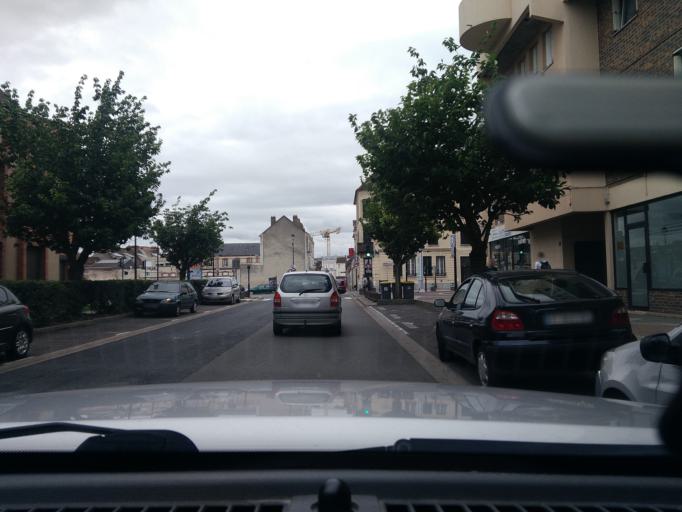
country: FR
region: Ile-de-France
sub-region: Departement de Seine-et-Marne
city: Montereau-Fault-Yonne
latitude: 48.3850
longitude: 2.9535
